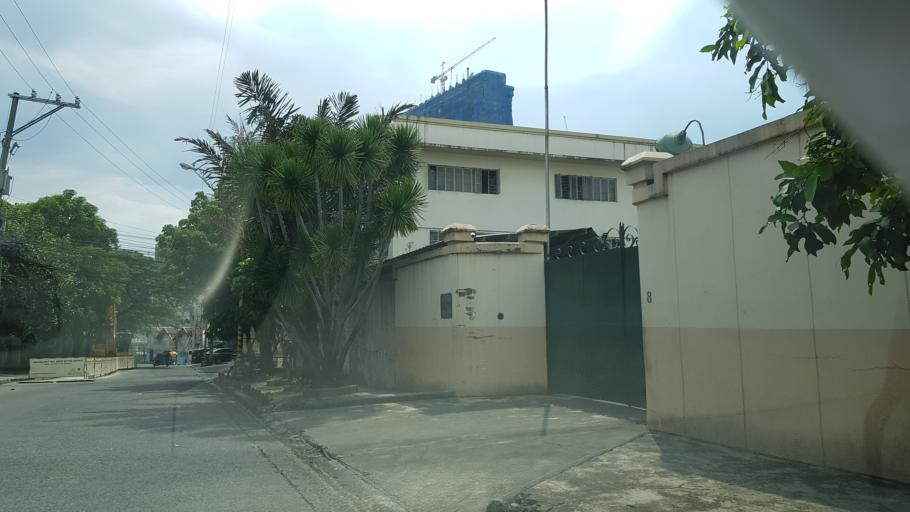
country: PH
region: Metro Manila
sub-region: Pasig
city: Pasig City
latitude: 14.5713
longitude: 121.0561
